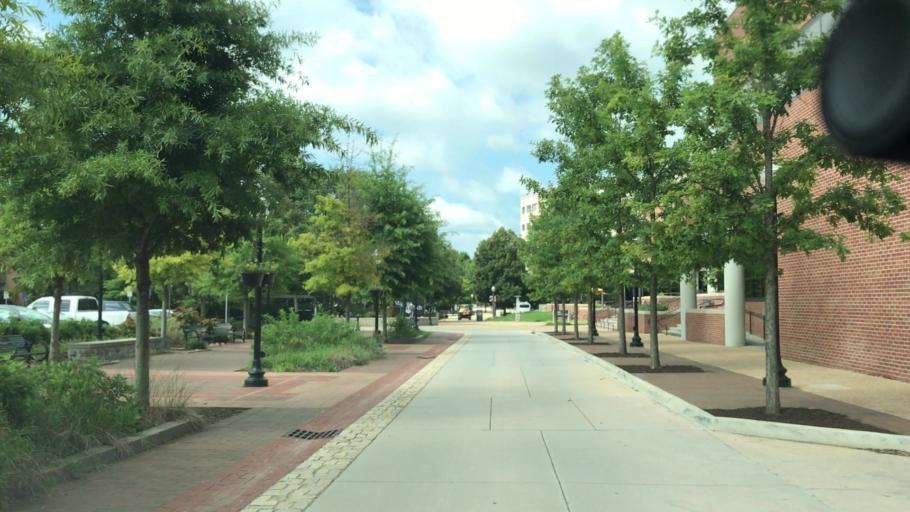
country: US
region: Virginia
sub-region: Montgomery County
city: Blacksburg
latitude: 37.2296
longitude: -80.4171
